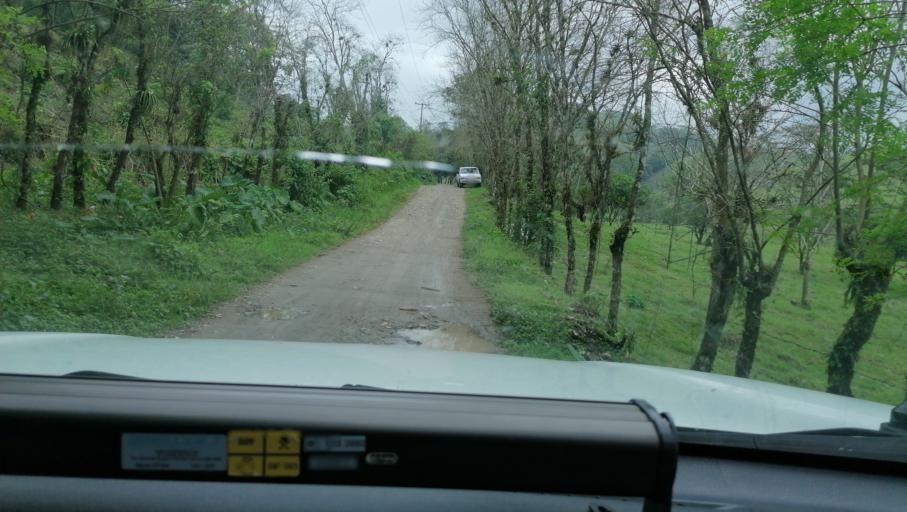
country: MX
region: Chiapas
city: Ixtacomitan
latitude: 17.3517
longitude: -93.1536
